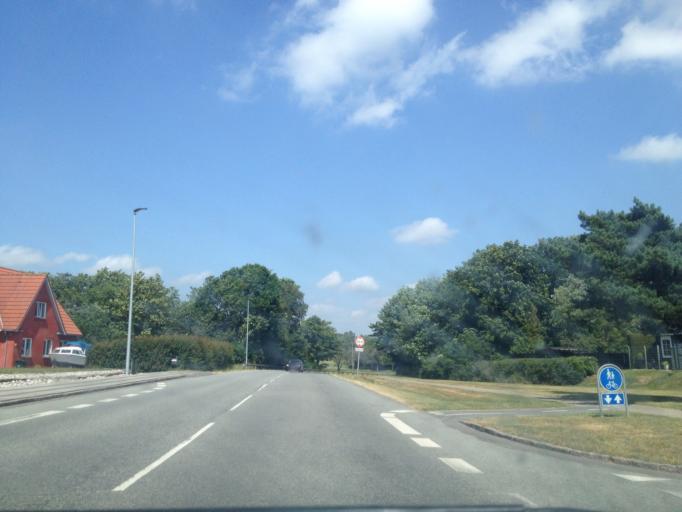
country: DK
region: South Denmark
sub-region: Kolding Kommune
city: Vamdrup
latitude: 55.4353
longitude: 9.2926
